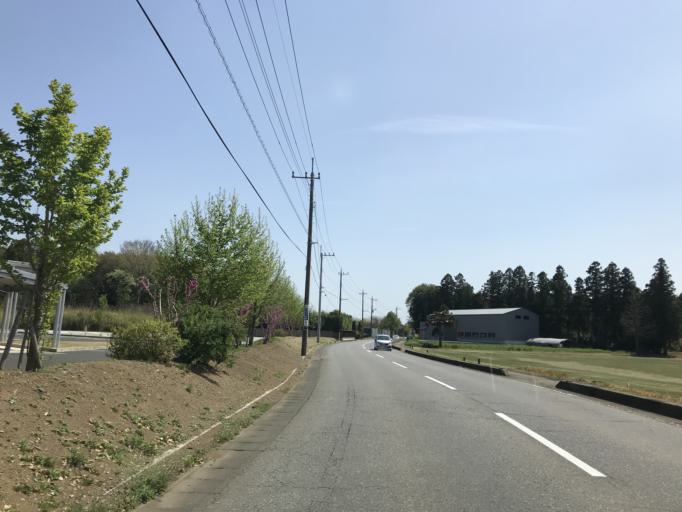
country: JP
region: Ibaraki
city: Naka
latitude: 36.0511
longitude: 140.0726
